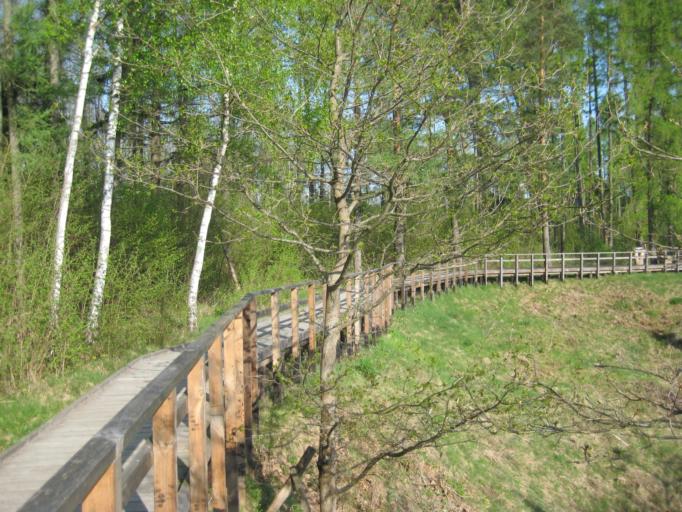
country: LT
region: Kauno apskritis
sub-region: Kauno rajonas
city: Karmelava
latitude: 54.8130
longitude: 24.1796
